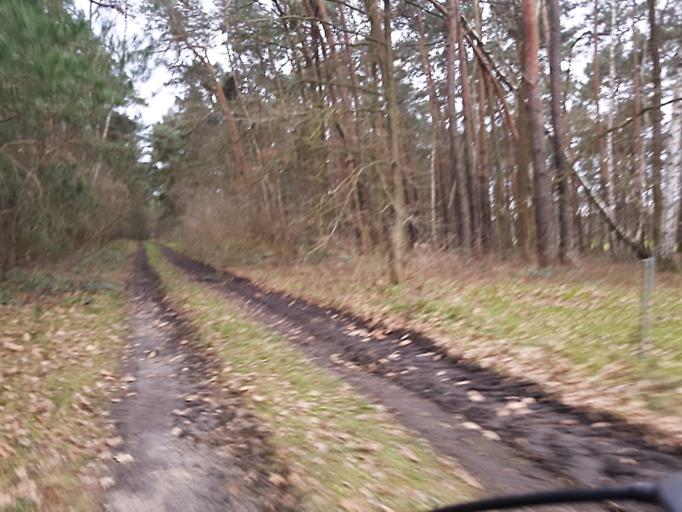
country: DE
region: Brandenburg
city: Schilda
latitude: 51.5779
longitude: 13.3985
